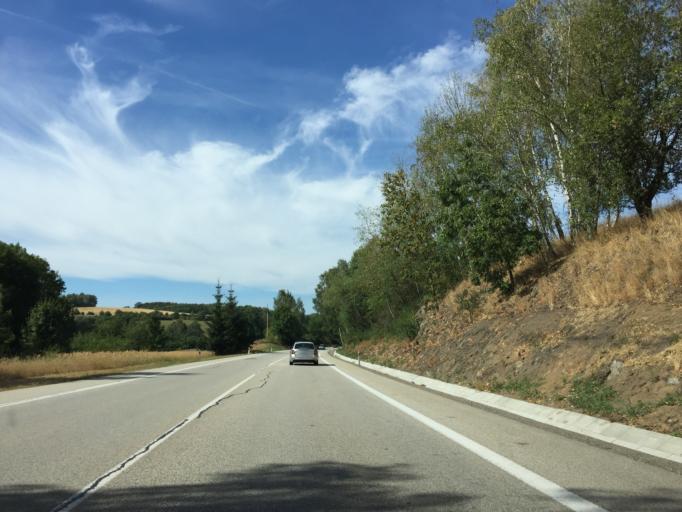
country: CZ
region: Central Bohemia
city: Votice
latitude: 49.6497
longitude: 14.6353
